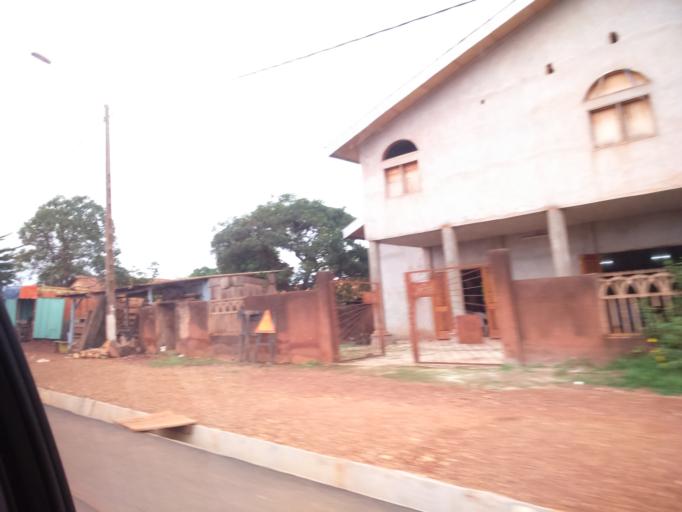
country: CI
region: Moyen-Comoe
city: Abengourou
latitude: 6.7250
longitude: -3.4868
